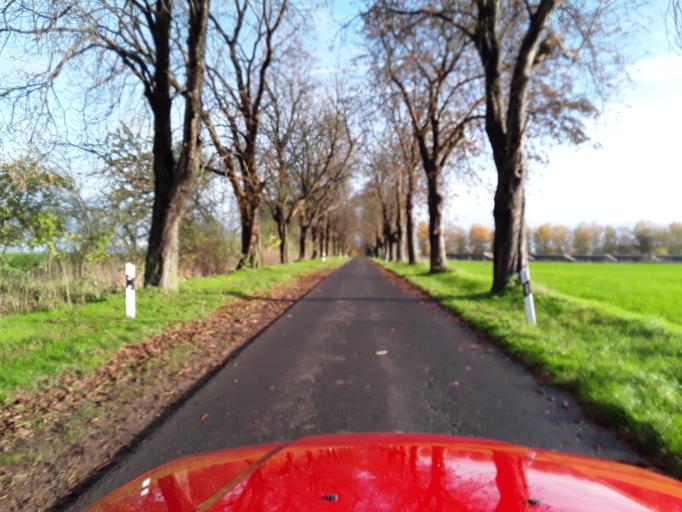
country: DE
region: Brandenburg
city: Mittenwalde
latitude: 53.2702
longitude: 13.6997
